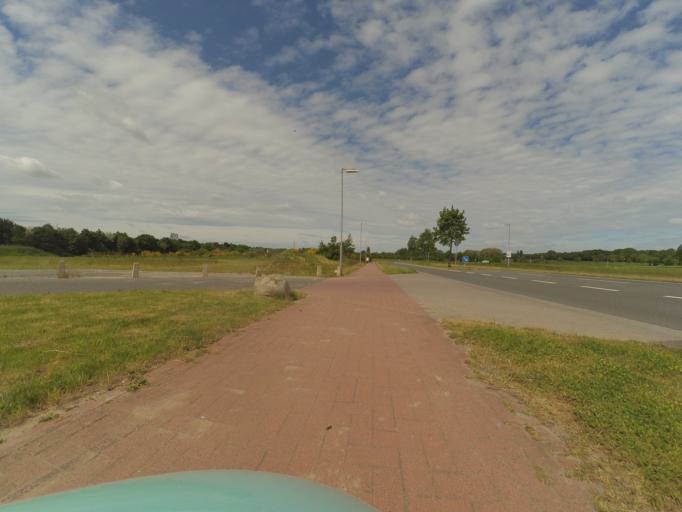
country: DE
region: Lower Saxony
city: Auf der Horst
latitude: 52.4246
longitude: 9.5930
